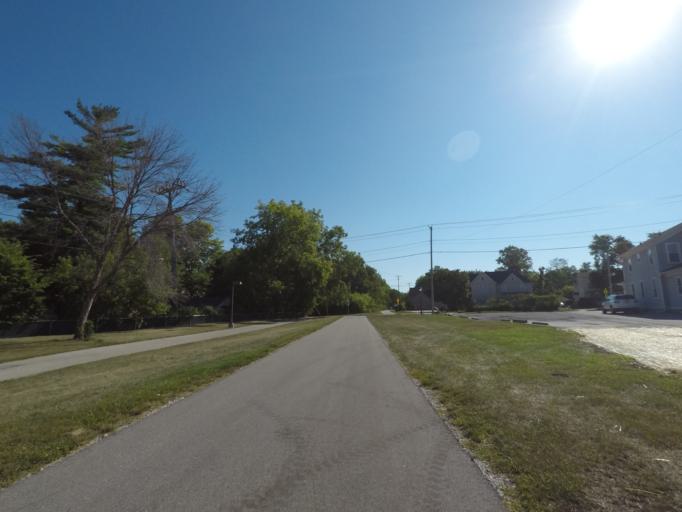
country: US
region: Wisconsin
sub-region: Waukesha County
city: Waukesha
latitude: 43.0063
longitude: -88.2275
